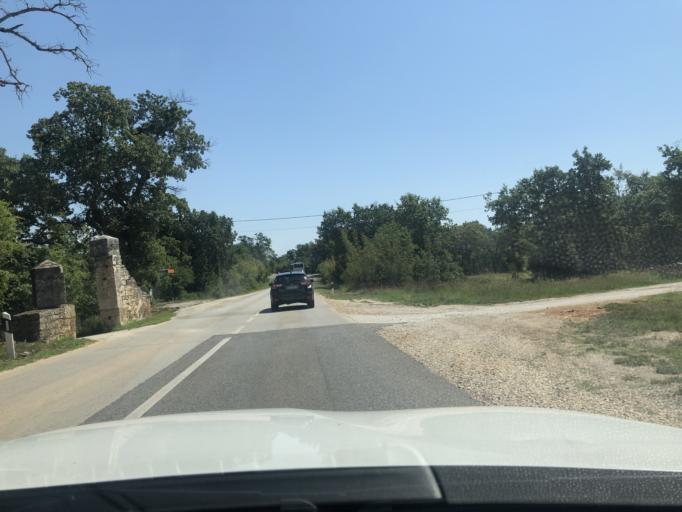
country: HR
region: Istarska
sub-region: Grad Rovinj
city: Rovinj
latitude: 45.0507
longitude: 13.7253
